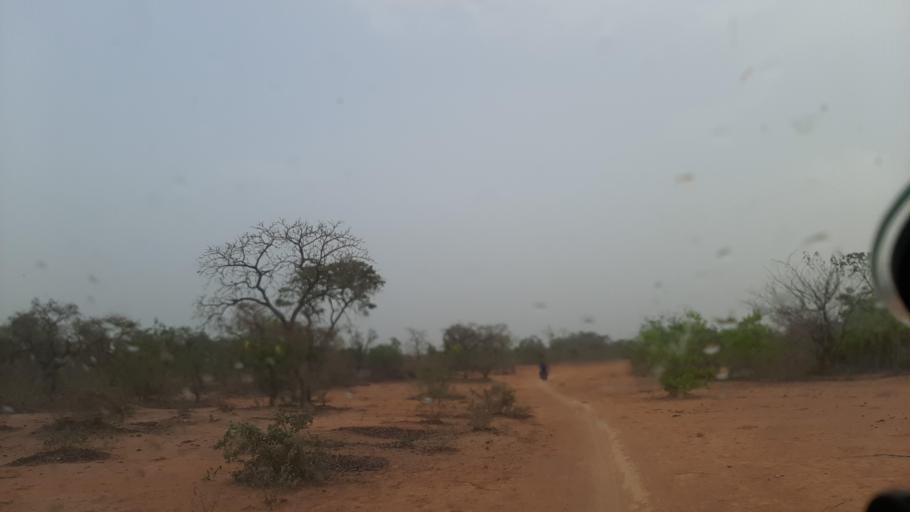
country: BF
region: Boucle du Mouhoun
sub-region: Province des Banwa
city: Salanso
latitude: 11.8650
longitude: -4.4418
